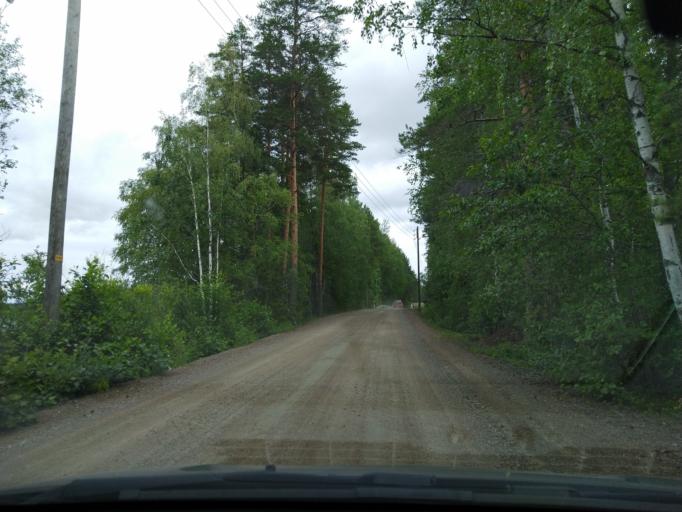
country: FI
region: Southern Savonia
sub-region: Mikkeli
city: Maentyharju
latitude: 61.1377
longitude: 26.8865
